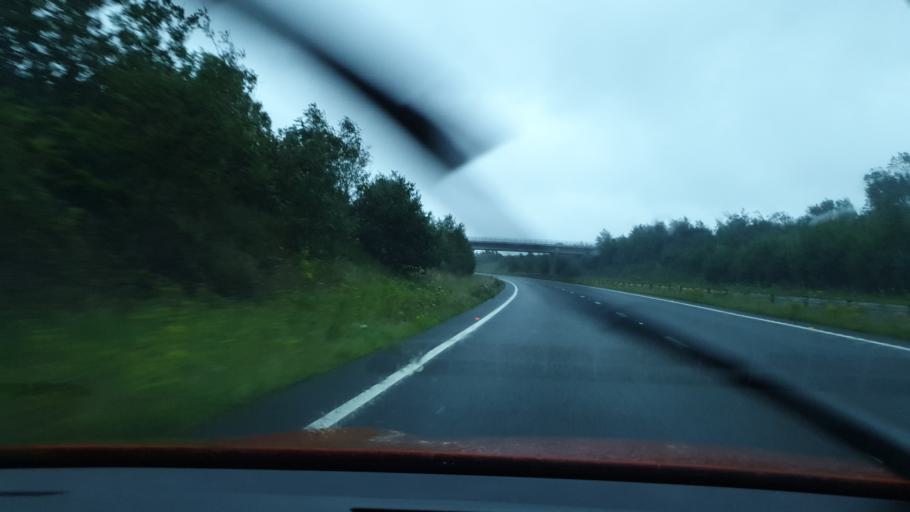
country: GB
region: England
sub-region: Cumbria
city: Grange-over-Sands
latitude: 54.2381
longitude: -2.9248
